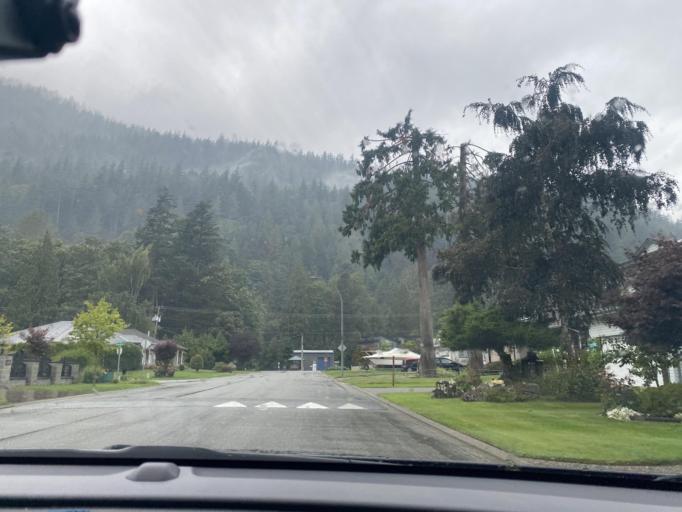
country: CA
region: British Columbia
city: Agassiz
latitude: 49.2964
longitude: -121.7826
